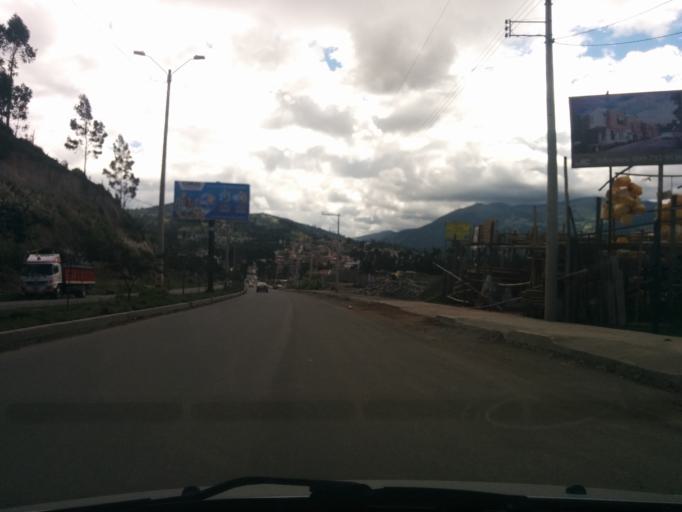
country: EC
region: Azuay
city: Cuenca
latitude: -2.9236
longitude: -79.0332
